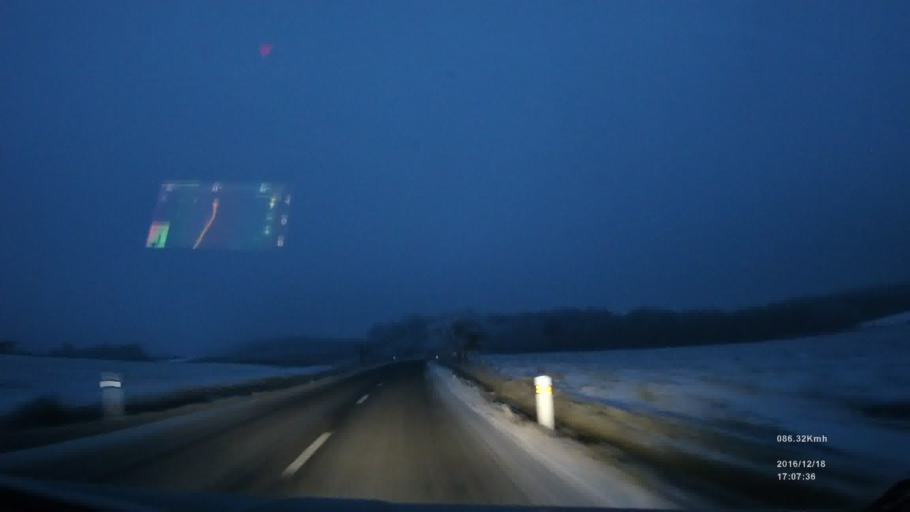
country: SK
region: Presovsky
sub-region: Okres Presov
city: Presov
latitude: 48.8946
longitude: 21.3187
